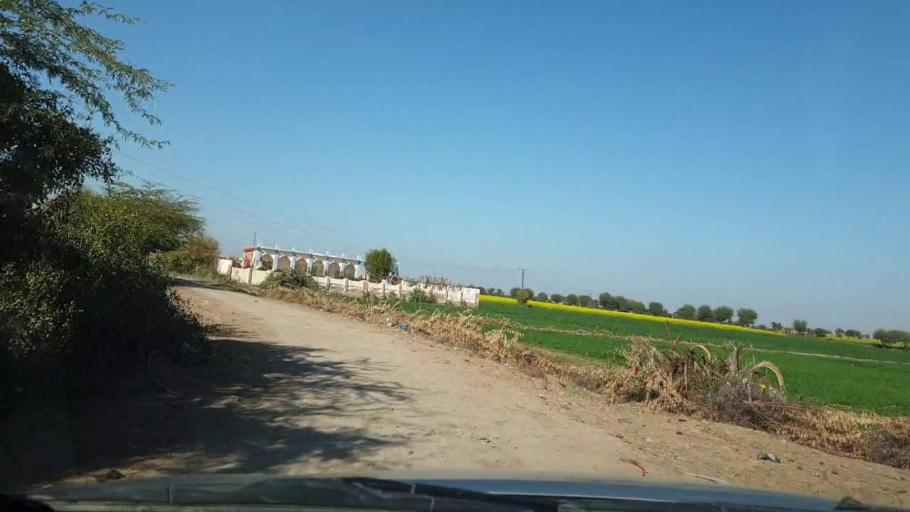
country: PK
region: Sindh
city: Berani
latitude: 25.8195
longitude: 68.9433
